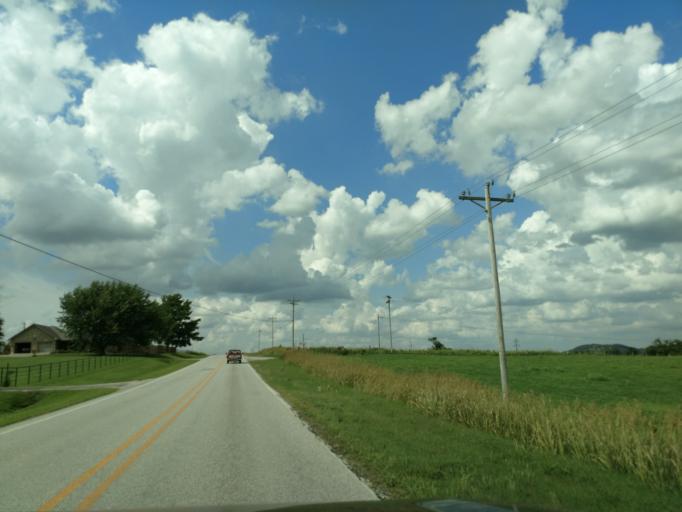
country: US
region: Arkansas
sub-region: Carroll County
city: Berryville
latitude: 36.4575
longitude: -93.5559
